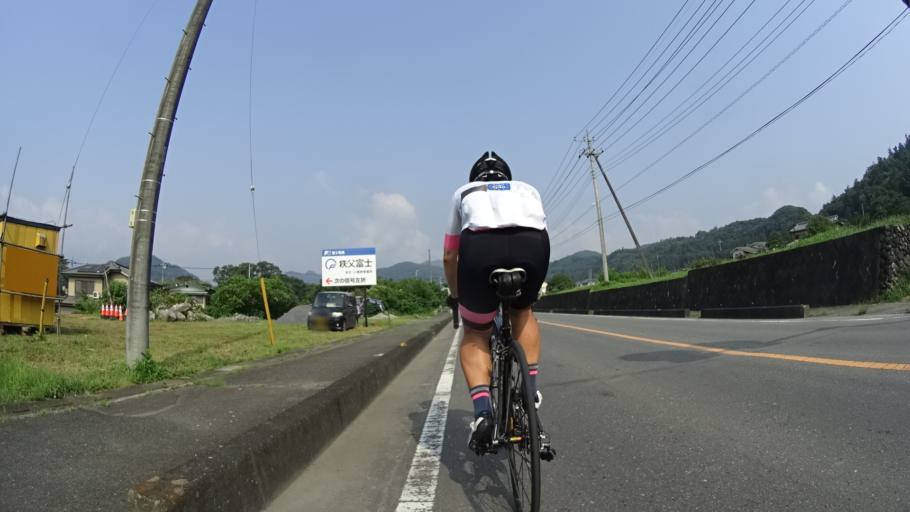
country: JP
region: Saitama
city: Chichibu
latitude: 36.0281
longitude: 138.9923
